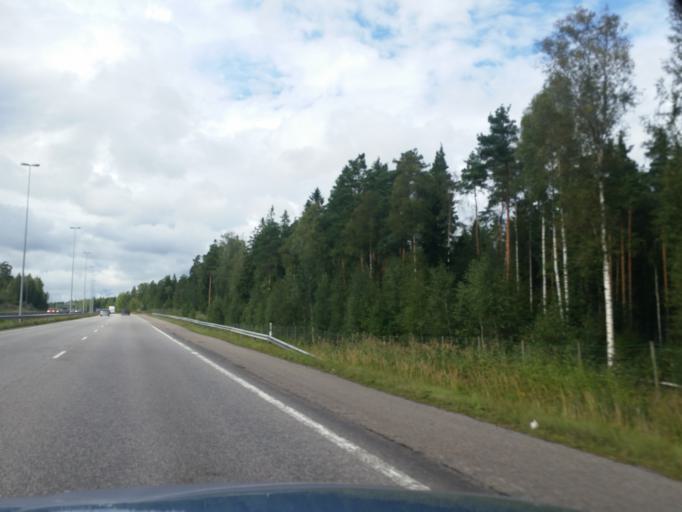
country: FI
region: Uusimaa
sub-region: Helsinki
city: Espoo
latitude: 60.2499
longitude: 24.5379
